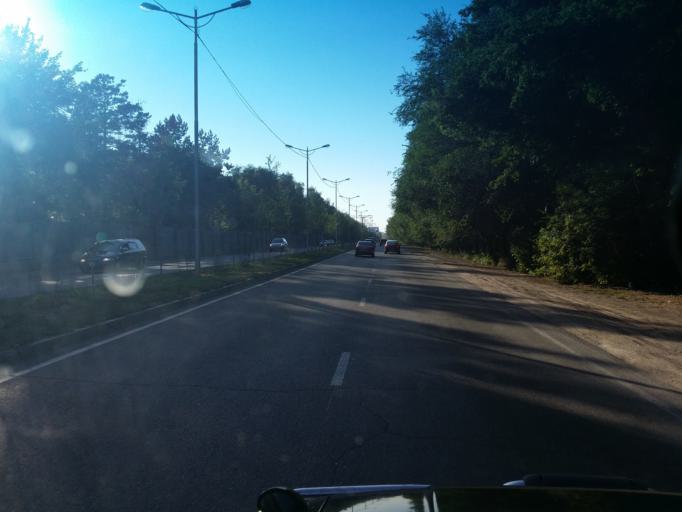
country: KZ
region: Almaty Oblysy
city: Pervomayskiy
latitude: 43.3211
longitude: 77.0238
